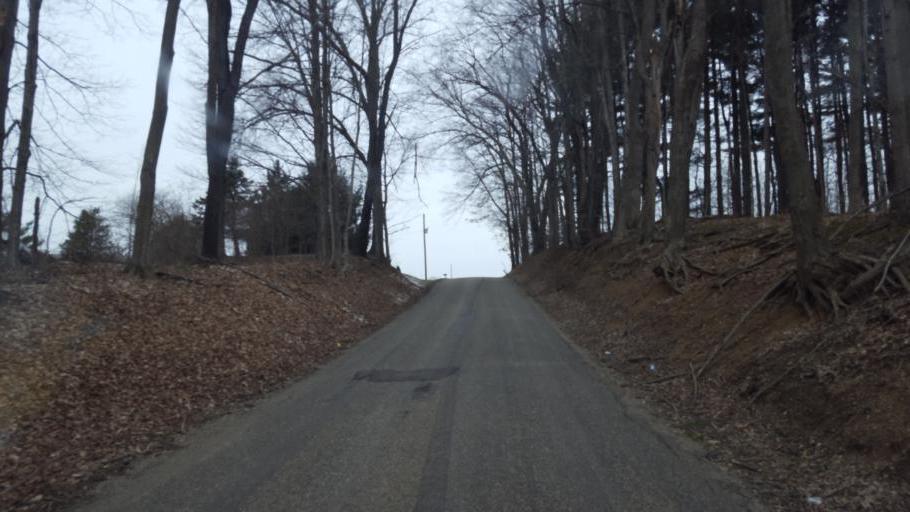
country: US
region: Ohio
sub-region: Sandusky County
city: Bellville
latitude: 40.5980
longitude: -82.4906
